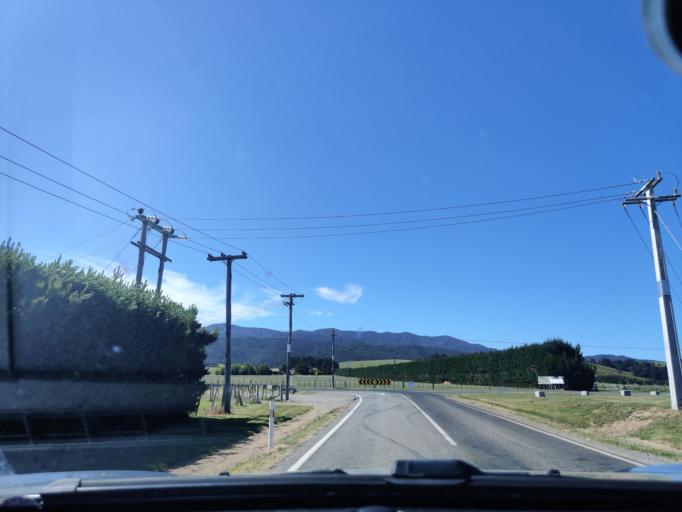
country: NZ
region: Wellington
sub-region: South Wairarapa District
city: Waipawa
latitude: -41.3053
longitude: 175.2733
